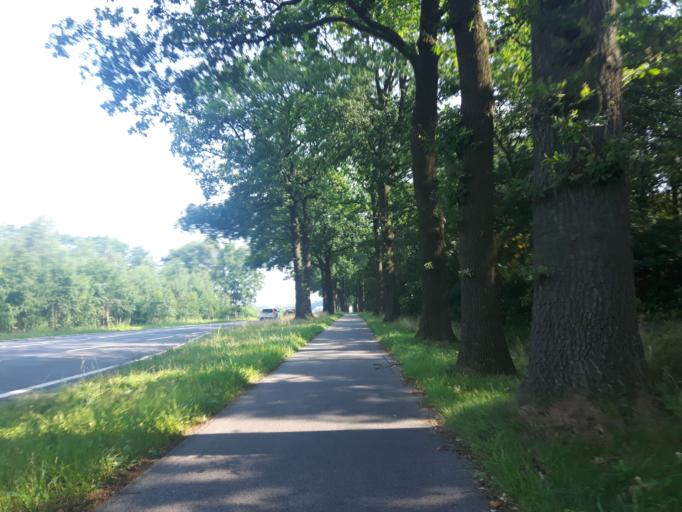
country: NL
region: Overijssel
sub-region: Gemeente Hof van Twente
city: Delden
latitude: 52.2189
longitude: 6.7459
